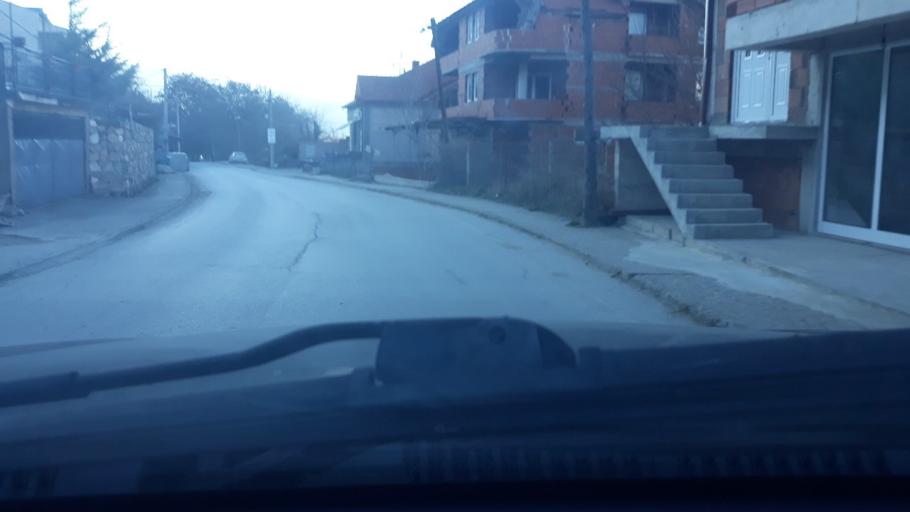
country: MK
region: Strumica
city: Strumica
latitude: 41.4384
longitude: 22.6289
